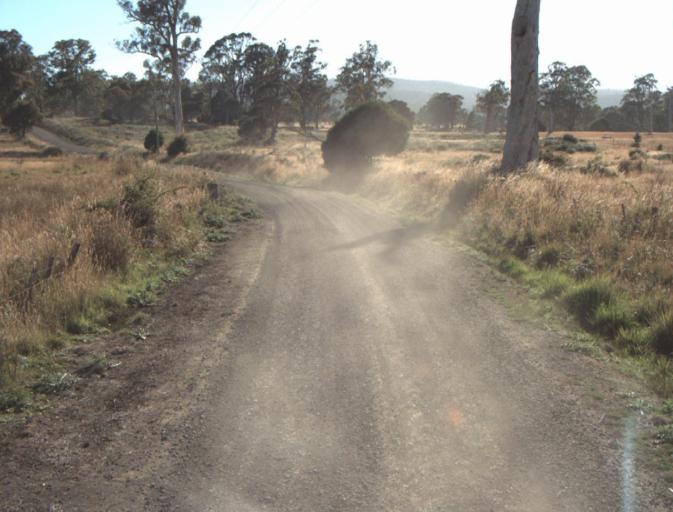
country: AU
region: Tasmania
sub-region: Launceston
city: Newstead
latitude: -41.4163
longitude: 147.2842
